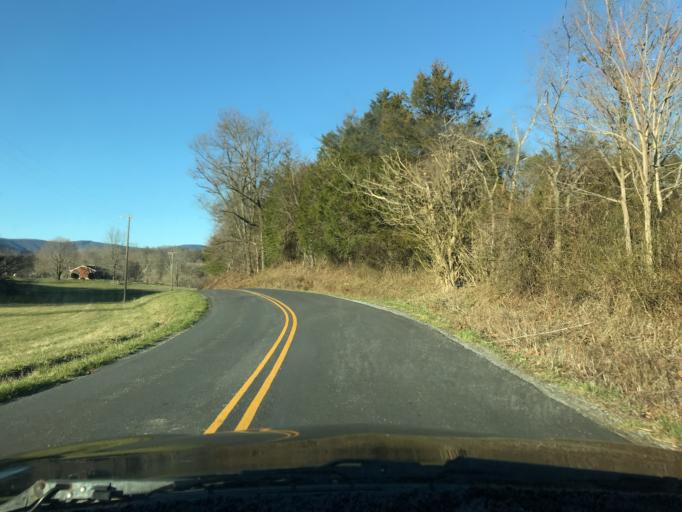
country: US
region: Virginia
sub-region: Botetourt County
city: Blue Ridge
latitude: 37.4128
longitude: -79.7025
